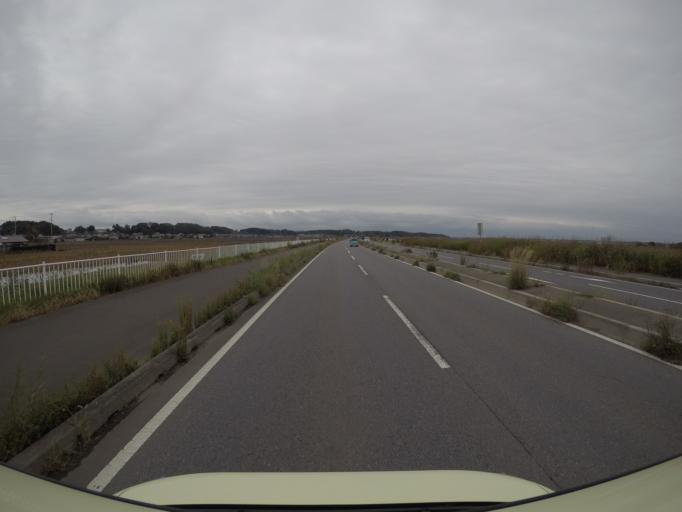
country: JP
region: Ibaraki
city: Ami
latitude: 36.0947
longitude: 140.2277
